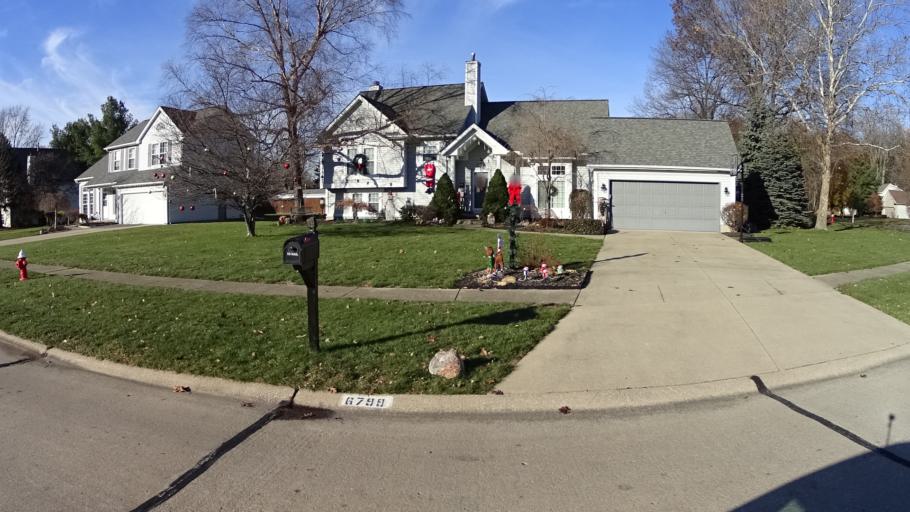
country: US
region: Ohio
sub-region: Lorain County
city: North Ridgeville
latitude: 41.3865
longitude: -81.9886
